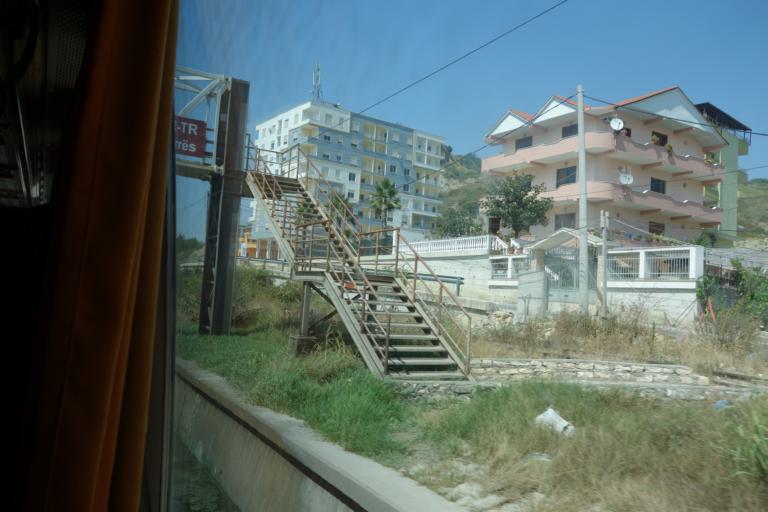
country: AL
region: Tirane
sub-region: Rrethi i Kavajes
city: Golem
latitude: 41.2770
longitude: 19.5158
